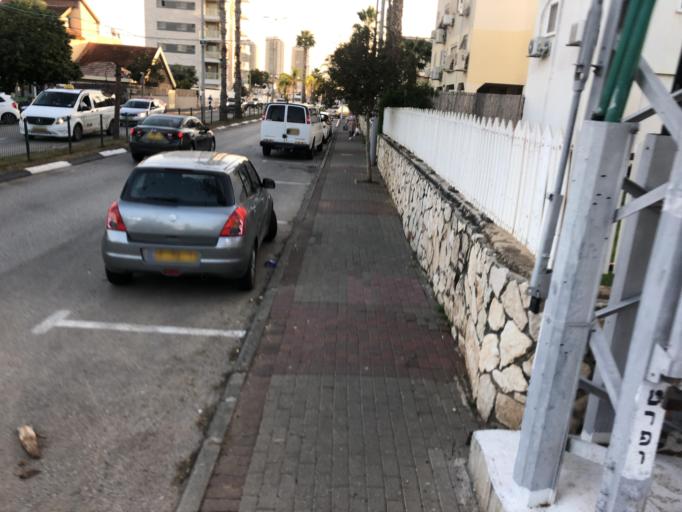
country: IL
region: Northern District
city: `Akko
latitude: 32.9267
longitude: 35.0920
